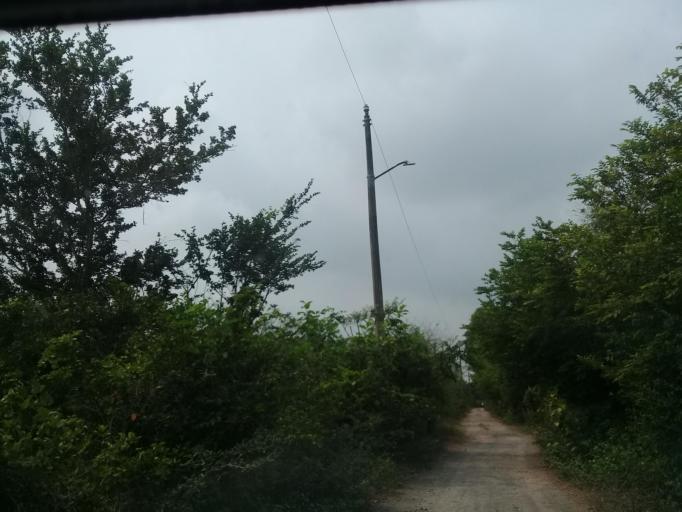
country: MX
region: Veracruz
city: El Tejar
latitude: 19.0591
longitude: -96.1915
